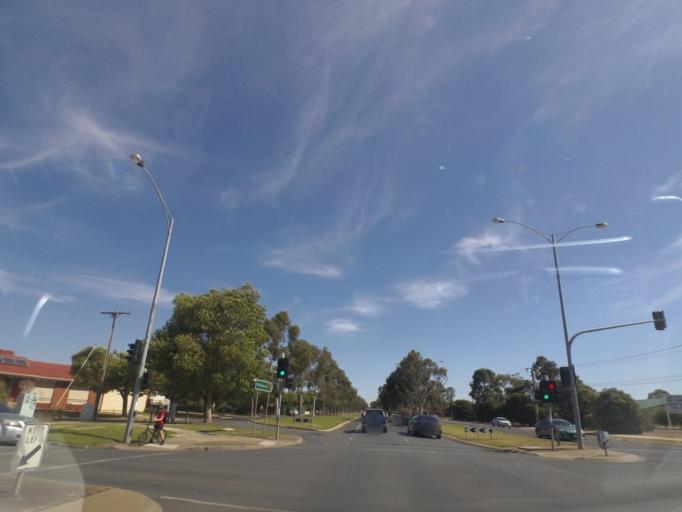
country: AU
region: Victoria
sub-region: Greater Shepparton
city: Shepparton
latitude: -36.3968
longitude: 145.3961
